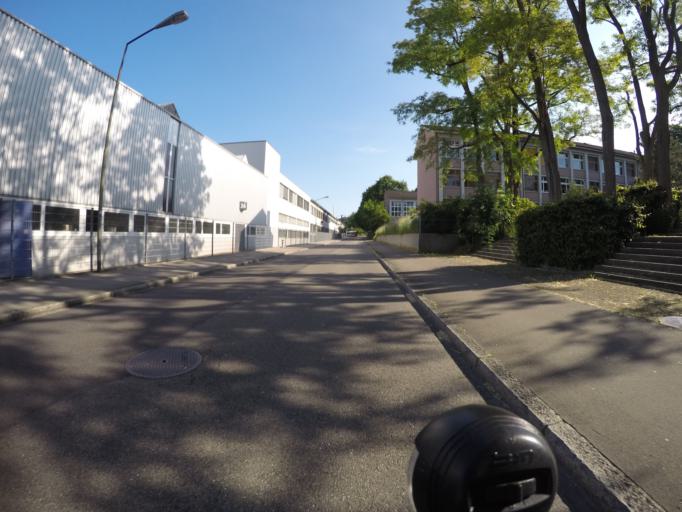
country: CH
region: Zurich
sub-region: Bezirk Winterthur
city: Toess (Kreis 4) / Eichliacker
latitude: 47.4858
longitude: 8.7084
